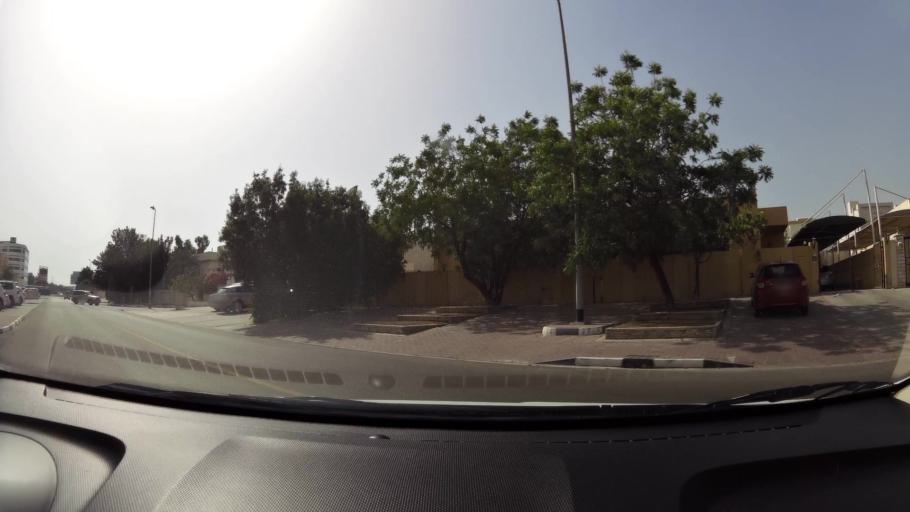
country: AE
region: Ash Shariqah
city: Sharjah
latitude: 25.2402
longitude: 55.3483
